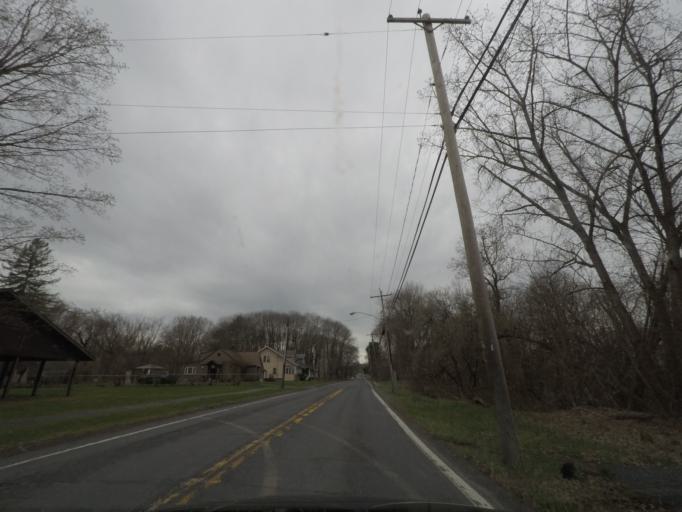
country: US
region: New York
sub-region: Albany County
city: Ravena
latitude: 42.5322
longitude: -73.8428
